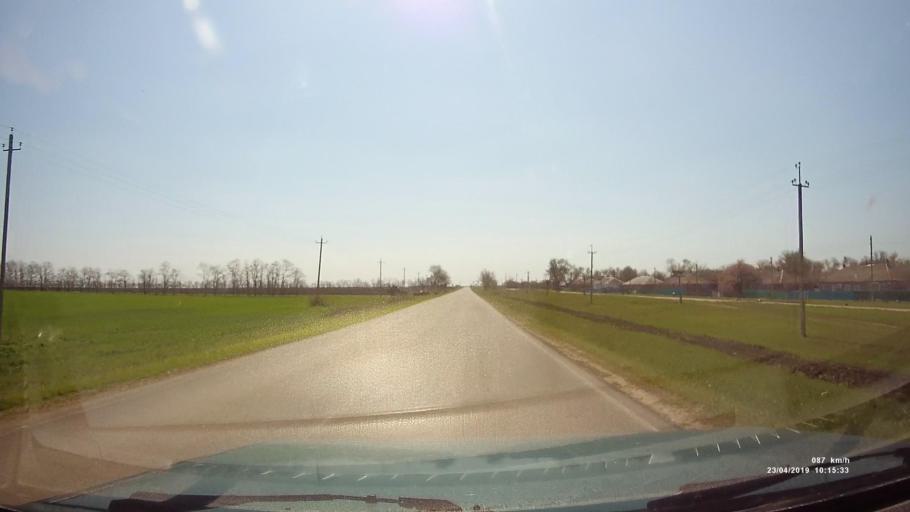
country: RU
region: Rostov
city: Sovetskoye
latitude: 46.6660
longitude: 42.3831
